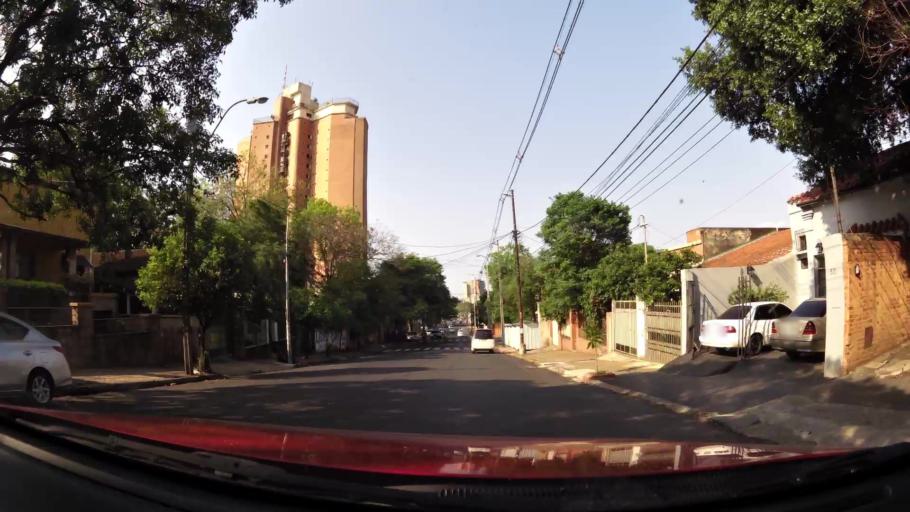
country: PY
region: Asuncion
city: Asuncion
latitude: -25.2945
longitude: -57.6229
